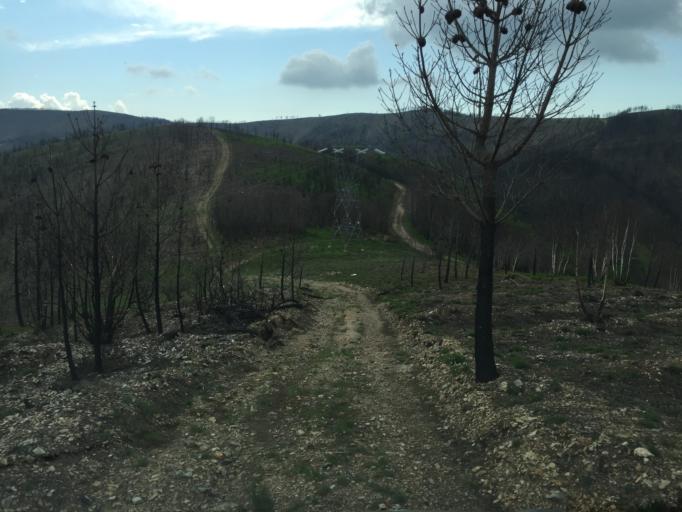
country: PT
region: Coimbra
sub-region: Arganil
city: Arganil
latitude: 40.1852
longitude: -7.9855
